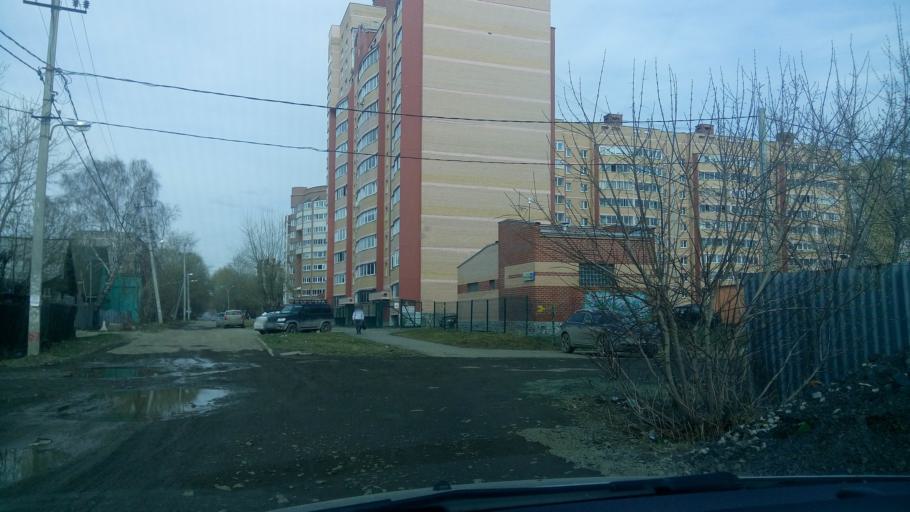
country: RU
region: Sverdlovsk
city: Yekaterinburg
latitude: 56.9078
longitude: 60.5857
